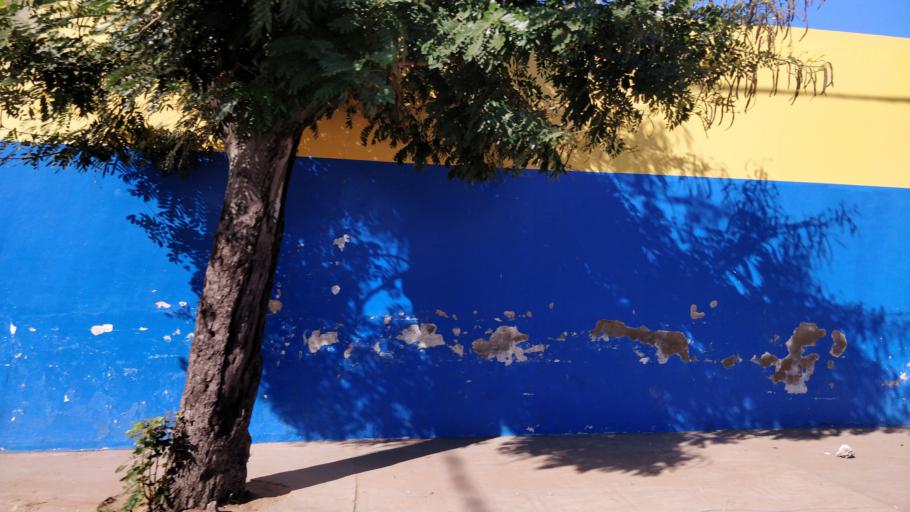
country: MZ
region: Maputo City
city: Maputo
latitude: -25.9278
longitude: 32.6019
